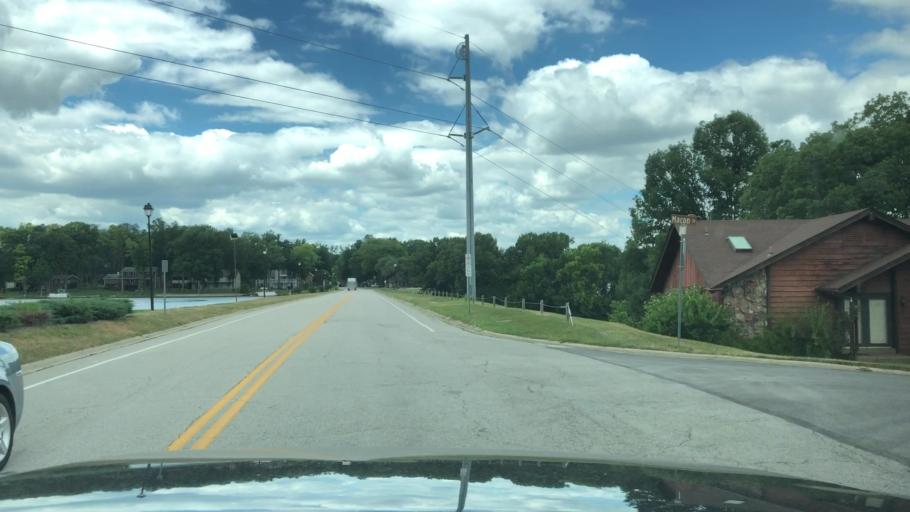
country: US
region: Missouri
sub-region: Saint Charles County
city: Lake Saint Louis
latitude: 38.7997
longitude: -90.7889
